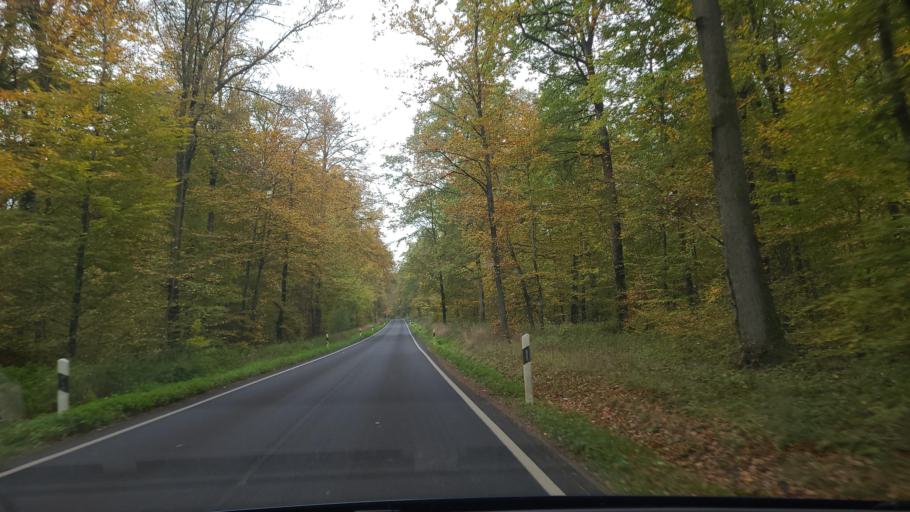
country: LU
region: Luxembourg
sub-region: Canton de Capellen
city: Dippach
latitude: 49.6014
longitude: 5.9953
